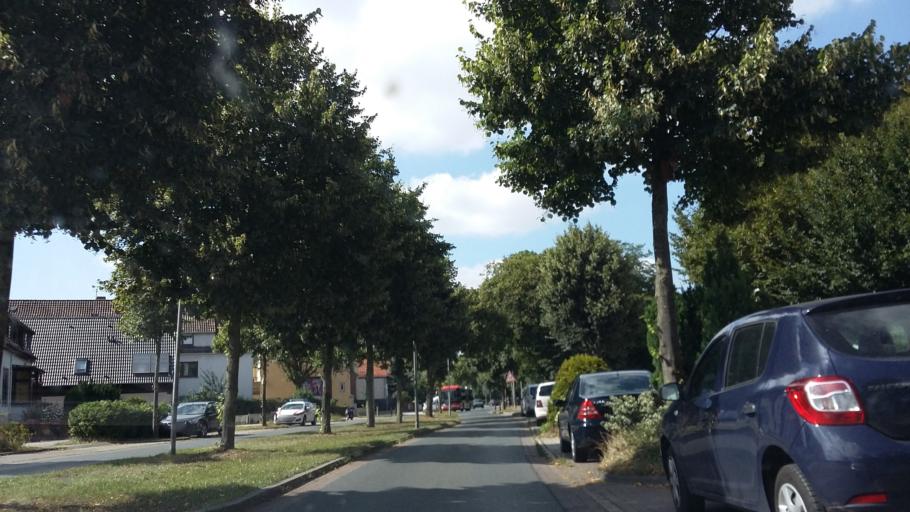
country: DE
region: Bremen
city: Bremen
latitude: 53.0452
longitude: 8.8214
